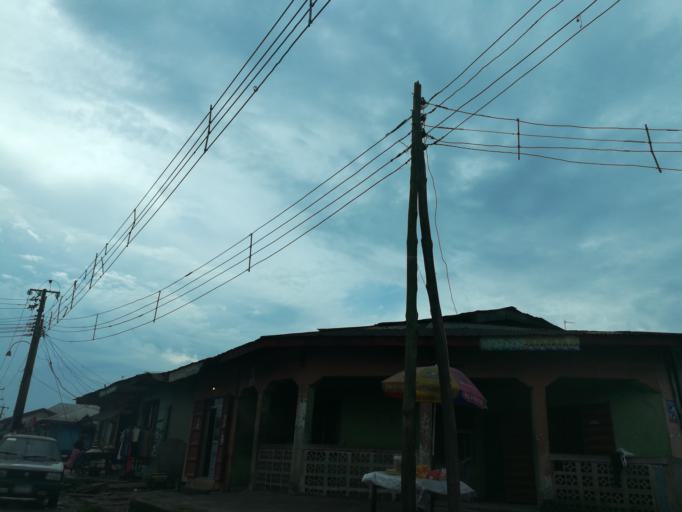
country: NG
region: Rivers
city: Port Harcourt
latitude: 4.7949
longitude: 6.9987
